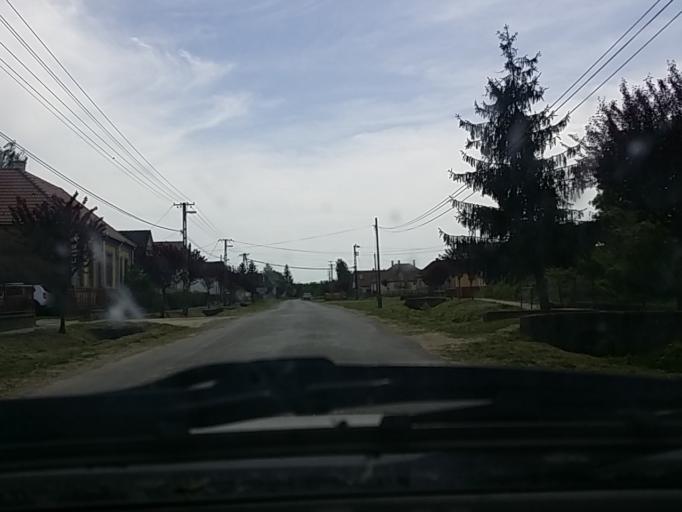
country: HU
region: Somogy
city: Barcs
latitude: 45.9767
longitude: 17.5890
